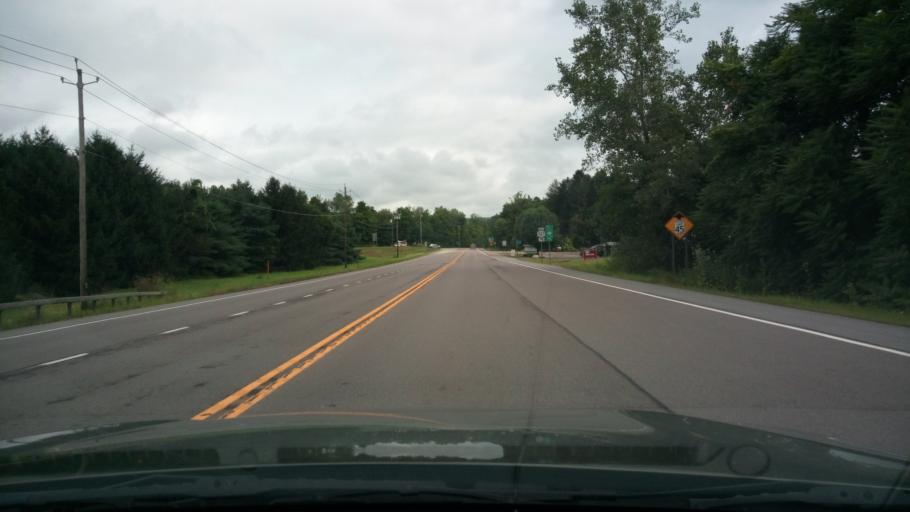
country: US
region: New York
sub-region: Tompkins County
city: South Hill
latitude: 42.4018
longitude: -76.5464
